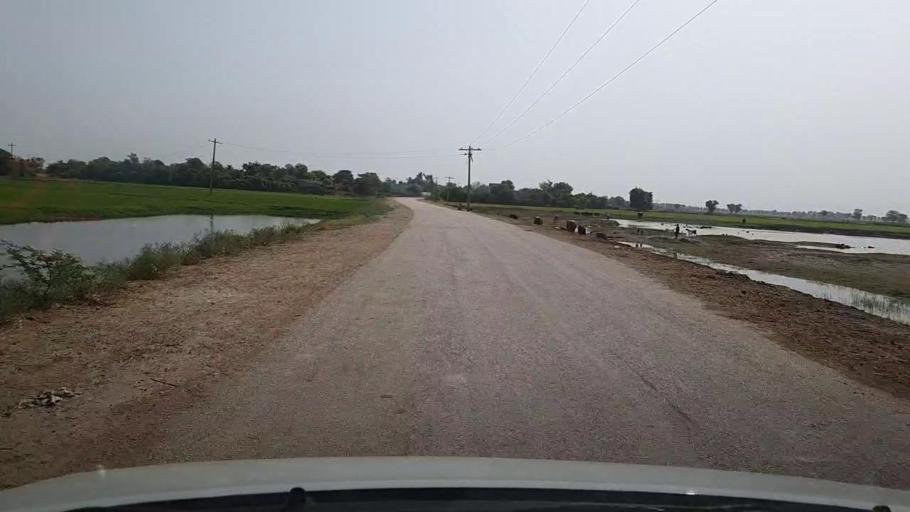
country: PK
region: Sindh
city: Mehar
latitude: 27.1196
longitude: 67.8441
